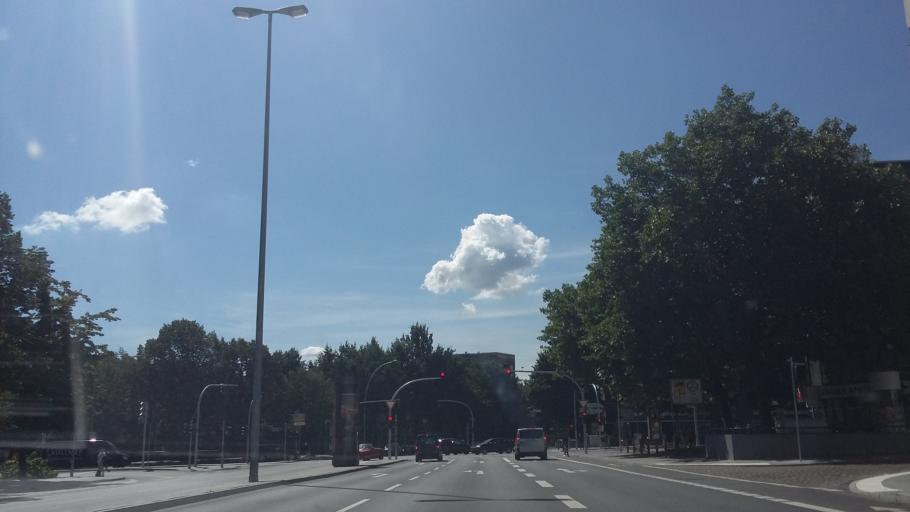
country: DE
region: Hamburg
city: St. Pauli
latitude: 53.5505
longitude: 9.9556
